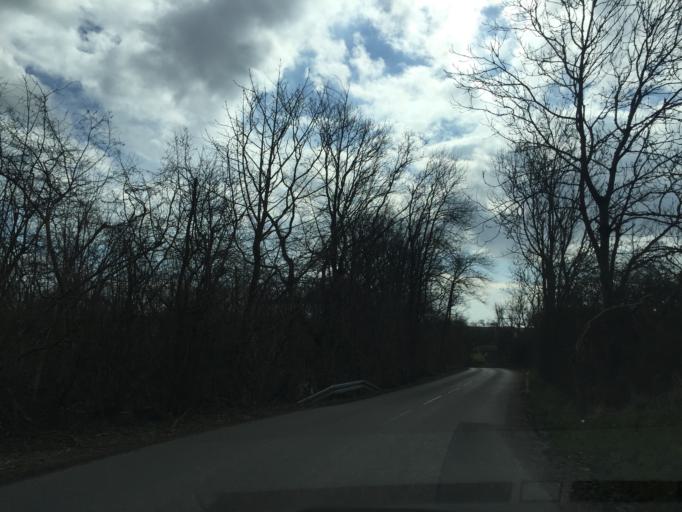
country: DK
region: South Denmark
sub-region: Svendborg Kommune
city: Svendborg
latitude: 55.0946
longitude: 10.5140
